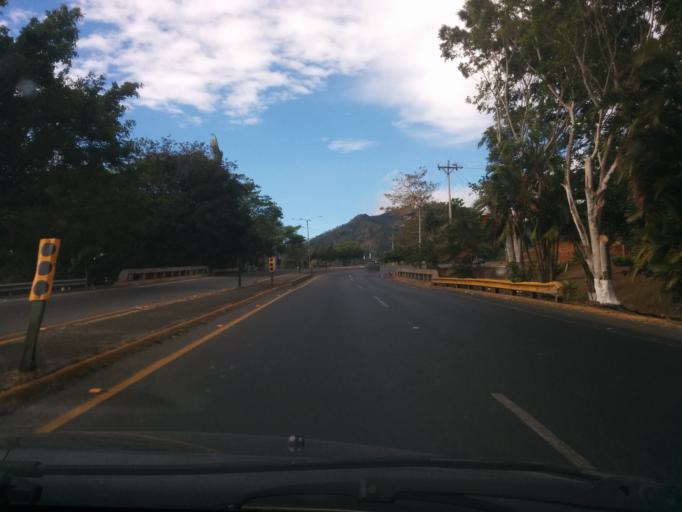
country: CR
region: Alajuela
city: Esquipulas
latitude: 10.0630
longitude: -84.4430
